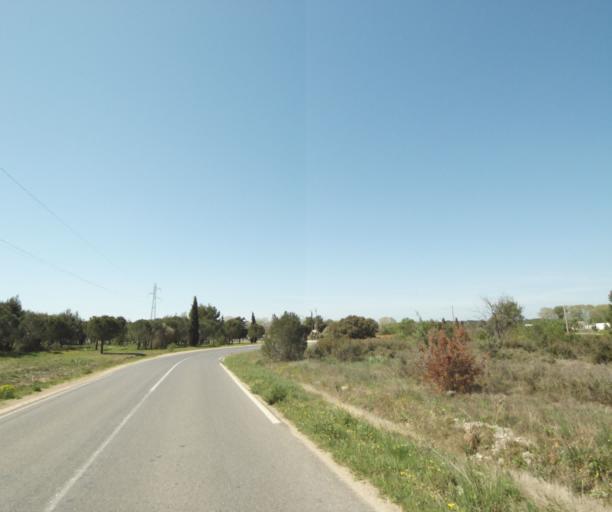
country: FR
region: Languedoc-Roussillon
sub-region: Departement de l'Herault
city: Saint-Bres
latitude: 43.6727
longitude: 4.0276
